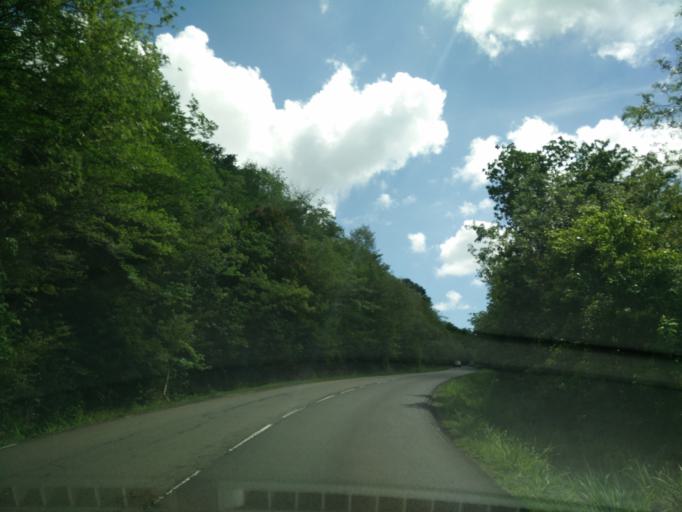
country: MQ
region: Martinique
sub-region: Martinique
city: Les Trois-Ilets
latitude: 14.5352
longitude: -61.0504
